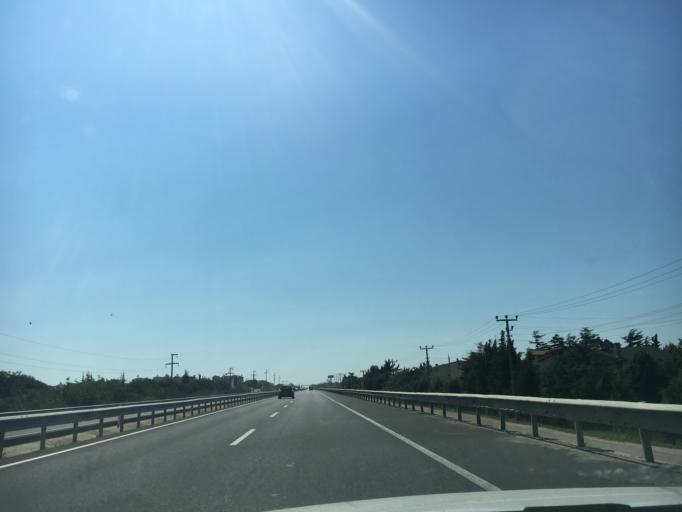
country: TR
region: Tekirdag
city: Marmara Ereglisi
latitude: 40.9852
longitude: 27.8579
